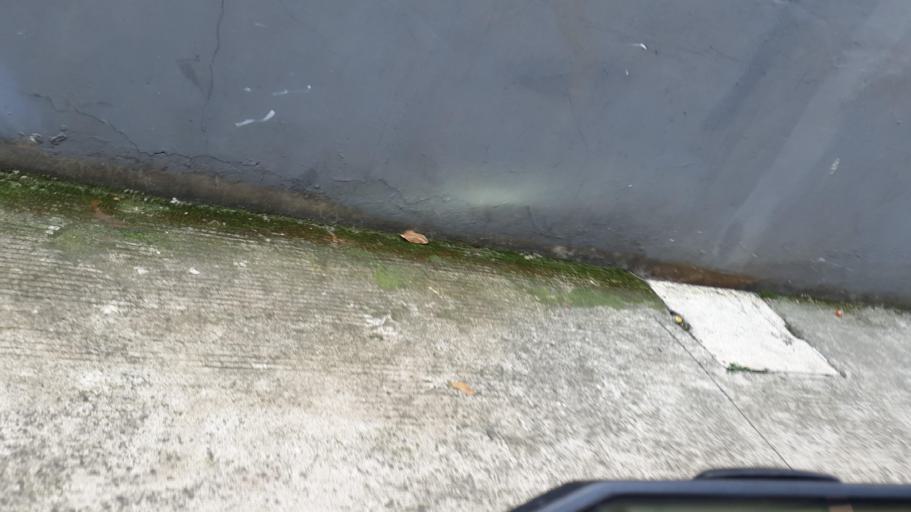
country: ID
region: West Java
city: Depok
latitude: -6.3620
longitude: 106.8344
